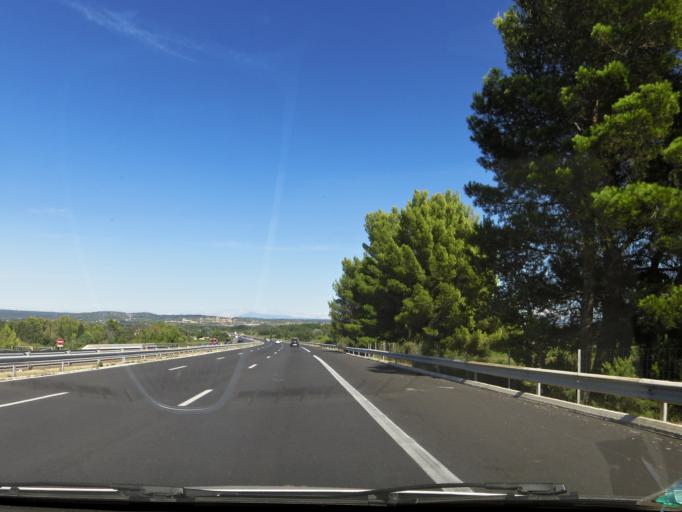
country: FR
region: Languedoc-Roussillon
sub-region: Departement du Gard
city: Sernhac
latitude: 43.9051
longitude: 4.5545
